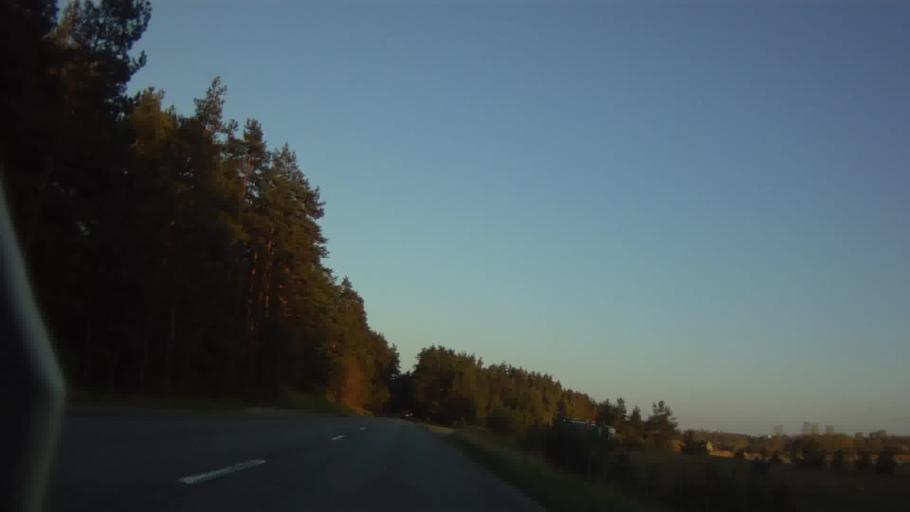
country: LV
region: Riga
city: Bergi
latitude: 57.0088
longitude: 24.2442
